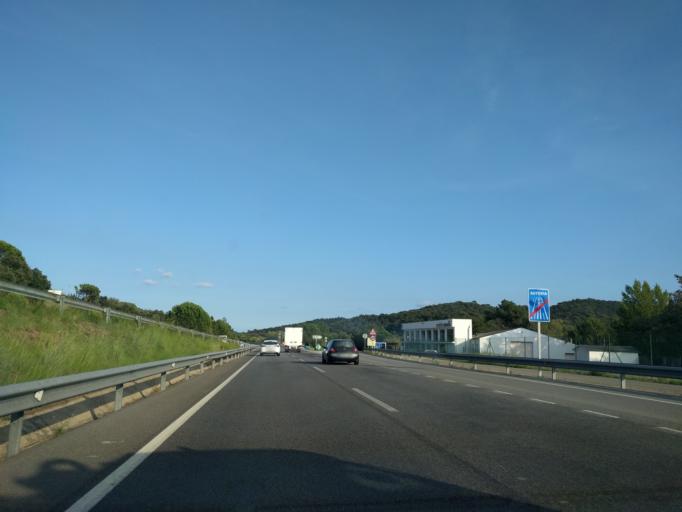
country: ES
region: Catalonia
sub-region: Provincia de Girona
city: Llagostera
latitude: 41.8277
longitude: 2.9431
